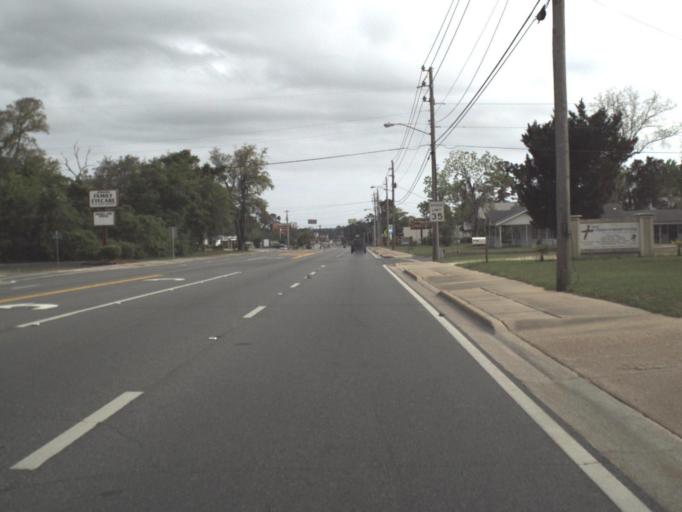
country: US
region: Florida
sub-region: Santa Rosa County
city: Milton
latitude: 30.6373
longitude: -87.0432
